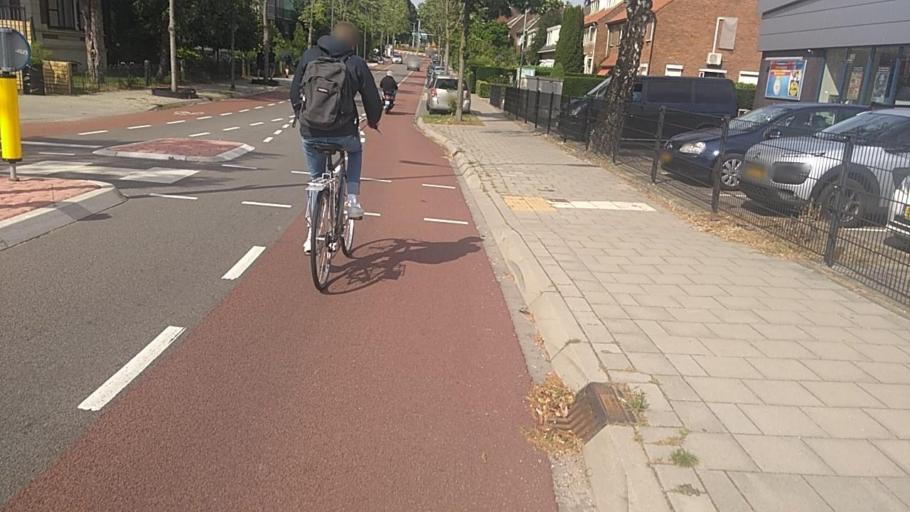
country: NL
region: Gelderland
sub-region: Gemeente Rheden
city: Velp
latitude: 51.9943
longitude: 5.9636
